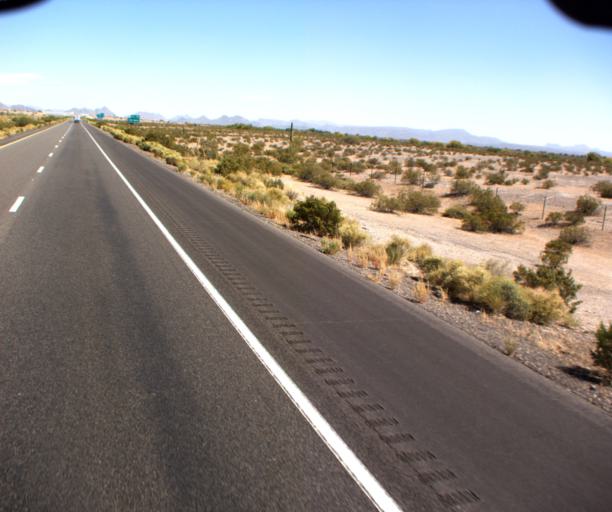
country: US
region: Arizona
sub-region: Maricopa County
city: Gila Bend
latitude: 32.9278
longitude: -112.6836
